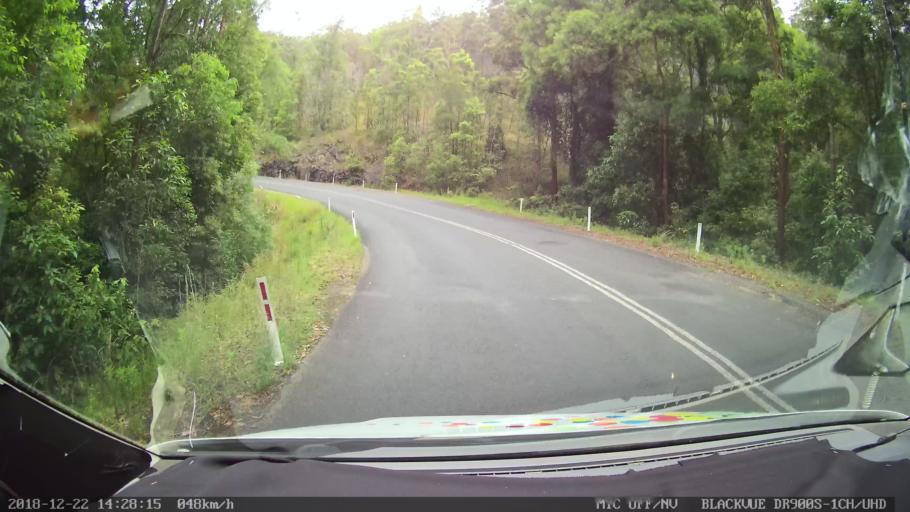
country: AU
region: New South Wales
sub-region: Bellingen
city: Dorrigo
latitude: -30.0720
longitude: 152.6354
